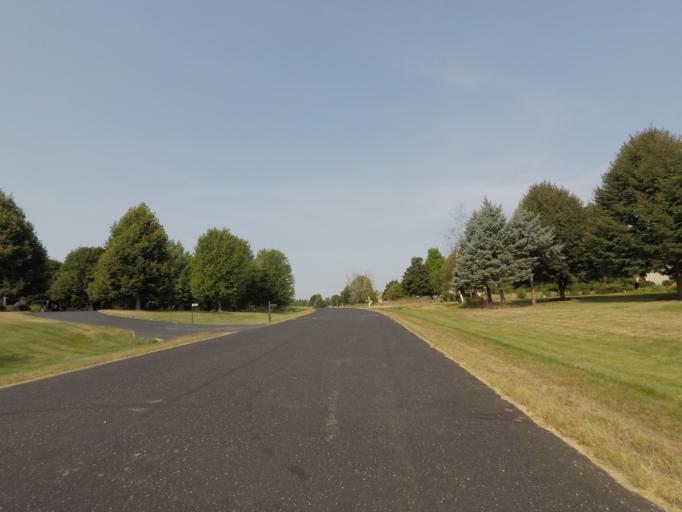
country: US
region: Wisconsin
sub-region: Waukesha County
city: Delafield
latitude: 43.0280
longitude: -88.4242
